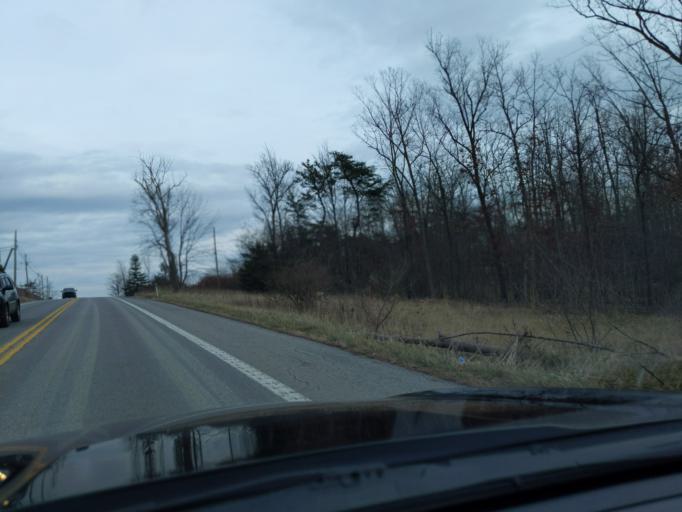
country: US
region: Pennsylvania
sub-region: Blair County
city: Lakemont
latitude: 40.4630
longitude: -78.3131
